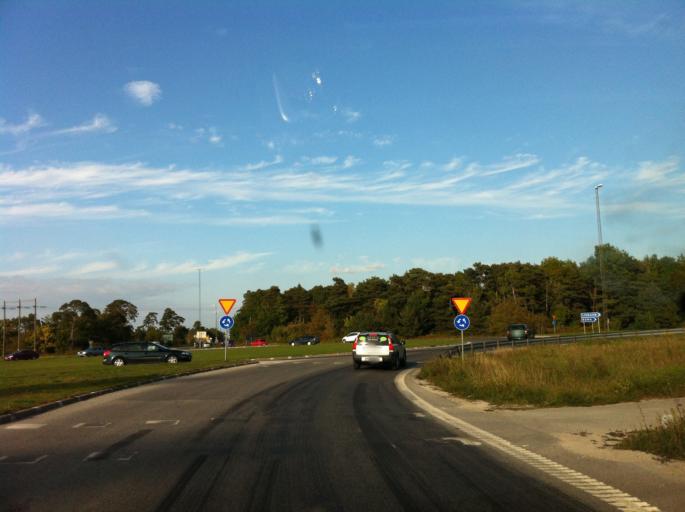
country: SE
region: Gotland
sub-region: Gotland
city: Visby
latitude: 57.6237
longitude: 18.3205
